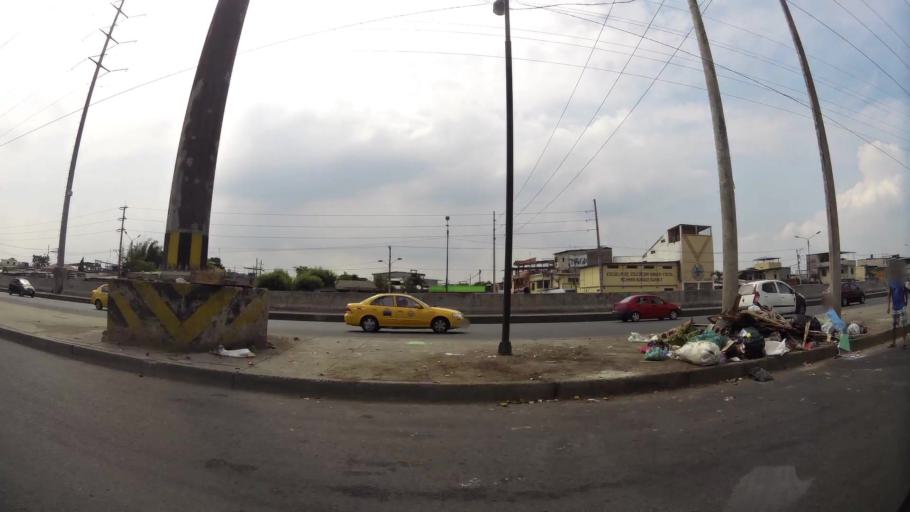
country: EC
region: Guayas
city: Guayaquil
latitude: -2.2402
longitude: -79.9181
